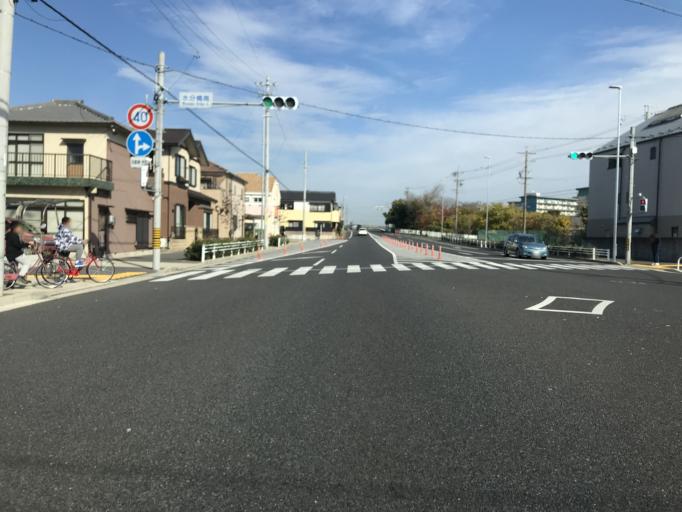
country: JP
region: Aichi
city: Nagoya-shi
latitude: 35.2124
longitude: 136.9325
